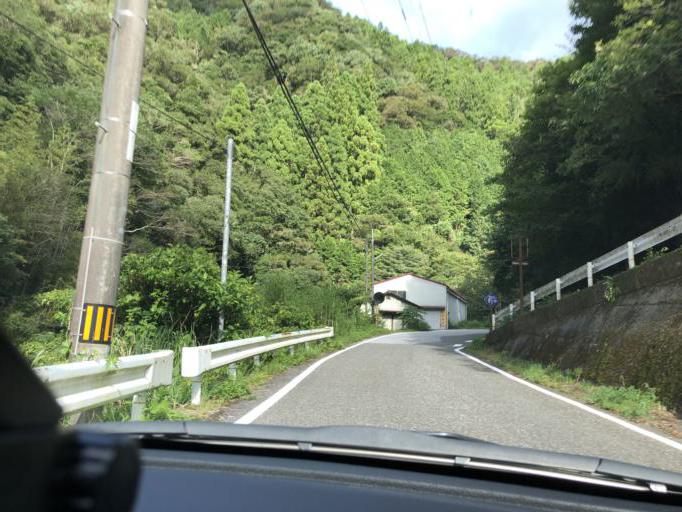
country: JP
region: Kochi
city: Kochi-shi
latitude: 33.6133
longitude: 133.4997
